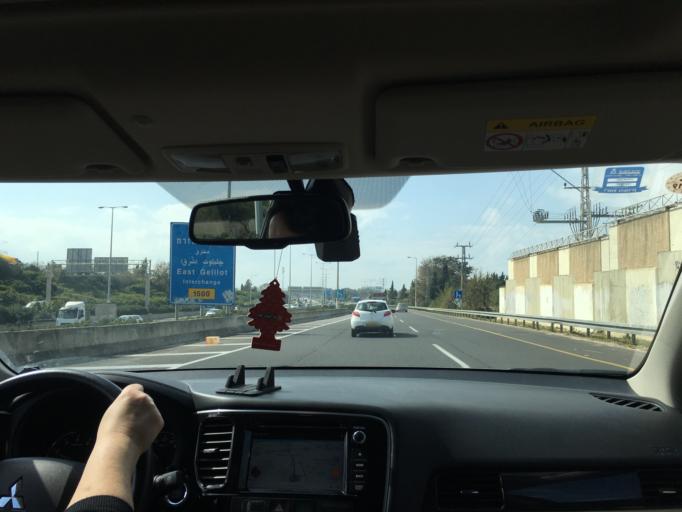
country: IL
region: Tel Aviv
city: Ramat HaSharon
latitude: 32.1364
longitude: 34.8308
